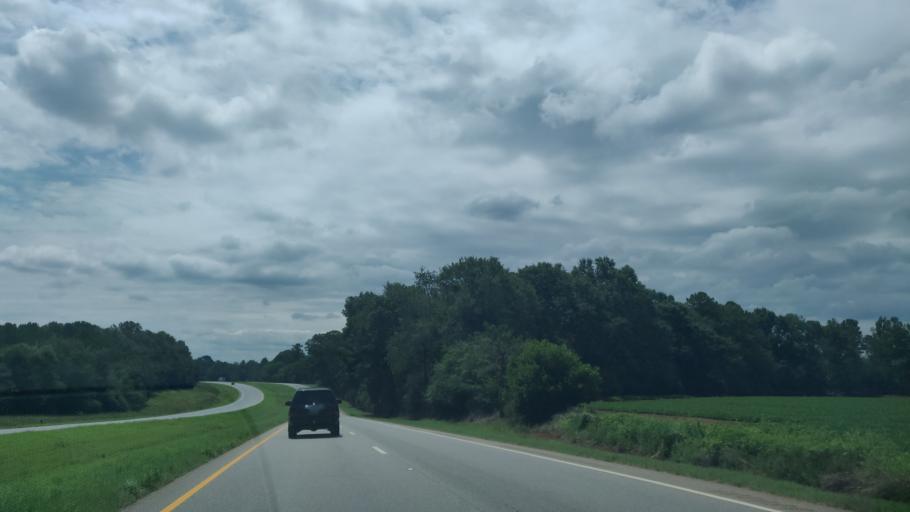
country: US
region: Georgia
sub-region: Terrell County
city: Dawson
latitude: 31.8754
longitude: -84.4968
